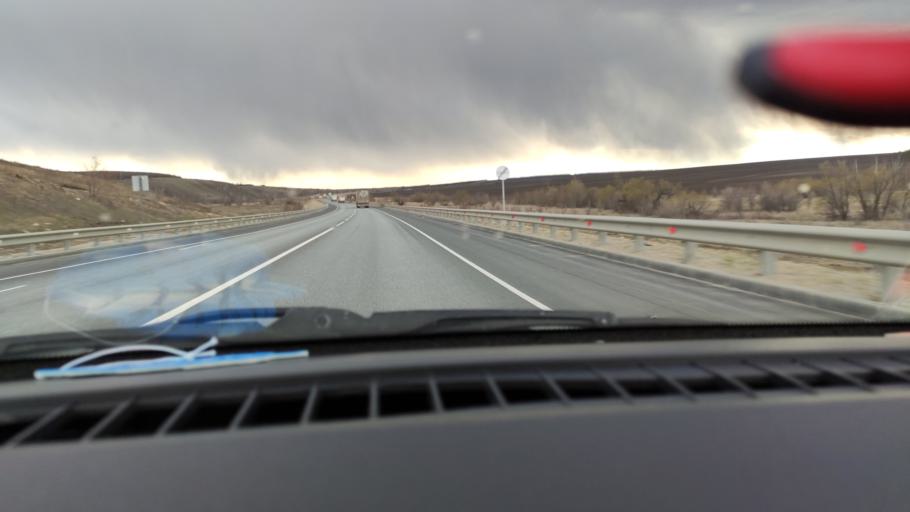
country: RU
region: Saratov
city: Yelshanka
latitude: 51.8683
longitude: 46.5025
